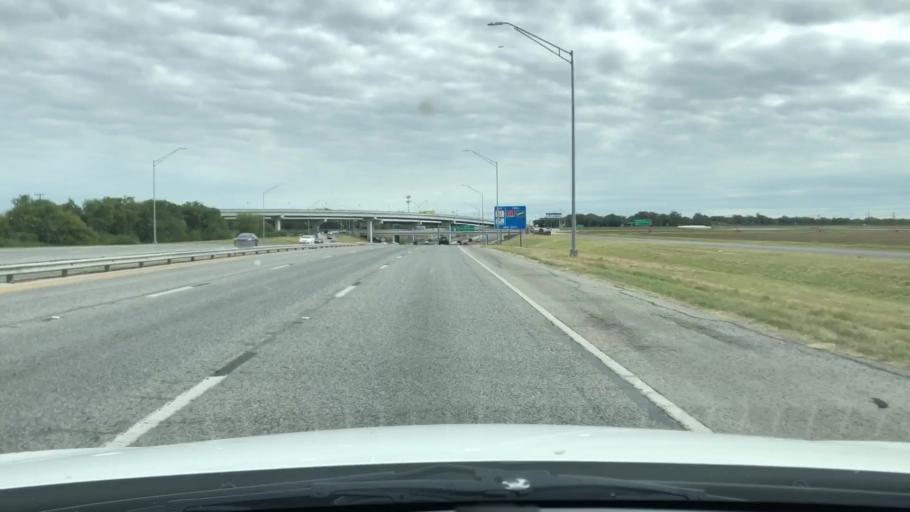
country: US
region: Texas
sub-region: Bexar County
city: Lackland Air Force Base
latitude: 29.4078
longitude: -98.5919
